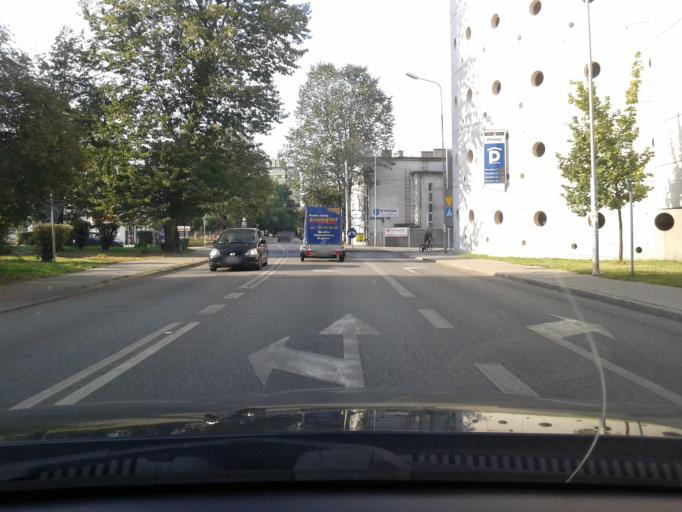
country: PL
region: Silesian Voivodeship
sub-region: Rybnik
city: Rybnik
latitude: 50.0961
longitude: 18.5365
